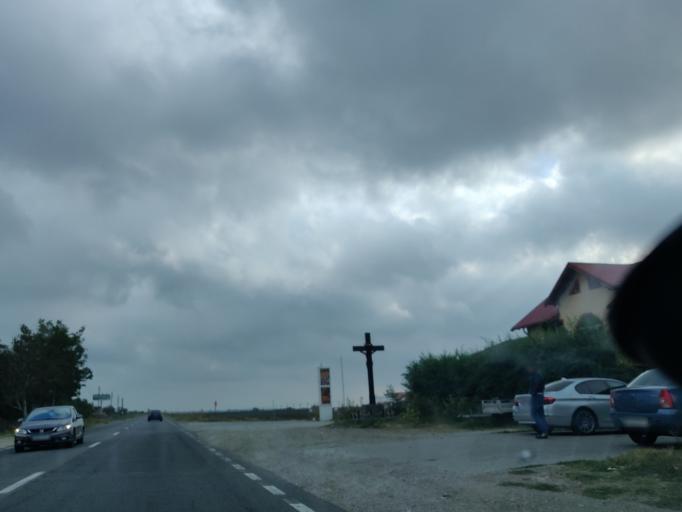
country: RO
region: Prahova
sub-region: Oras Mizil
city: Mizil
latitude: 45.0086
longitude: 26.4600
